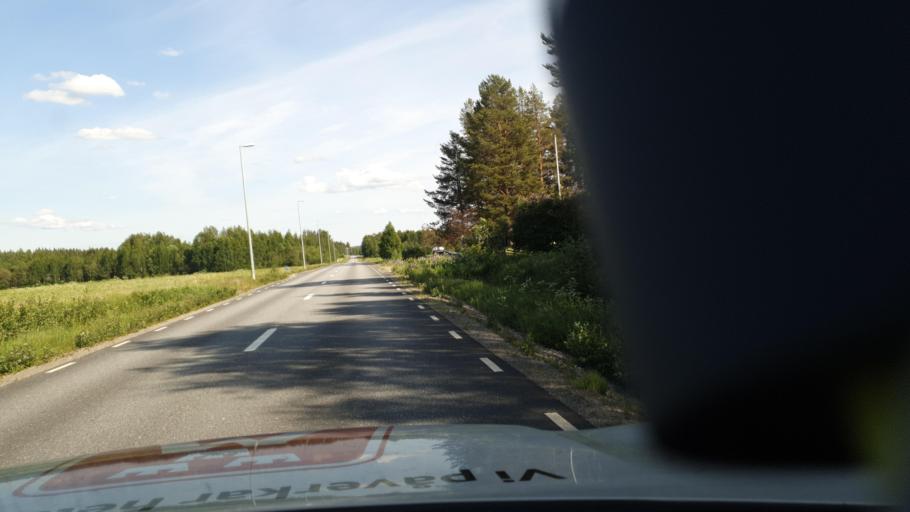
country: SE
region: Vaesterbotten
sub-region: Skelleftea Kommun
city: Forsbacka
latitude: 64.6983
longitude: 20.4753
